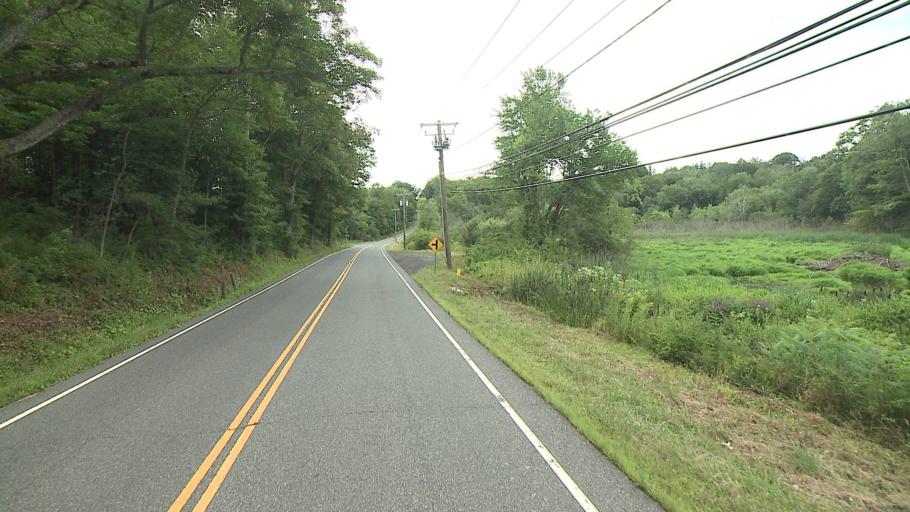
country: US
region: Connecticut
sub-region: Litchfield County
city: New Preston
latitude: 41.6206
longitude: -73.2961
